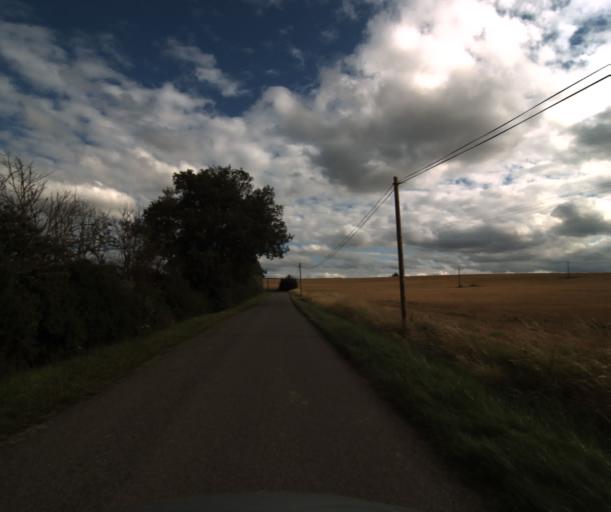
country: FR
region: Midi-Pyrenees
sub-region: Departement de la Haute-Garonne
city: Le Fauga
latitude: 43.4043
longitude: 1.3230
